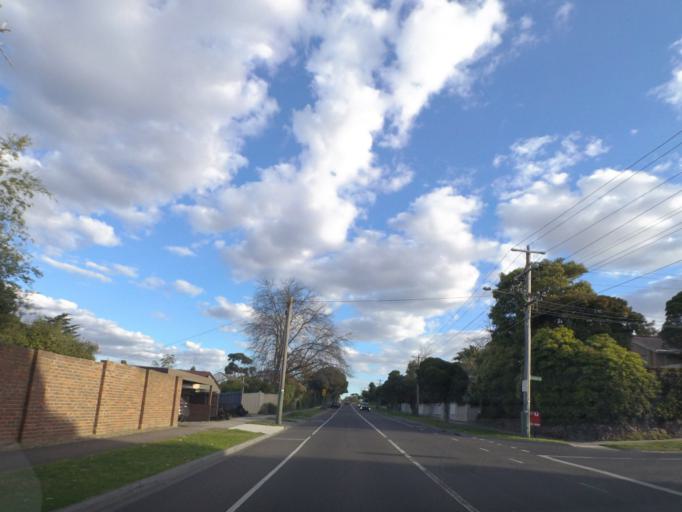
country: AU
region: Victoria
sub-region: Boroondara
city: Balwyn North
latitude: -37.7992
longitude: 145.0980
